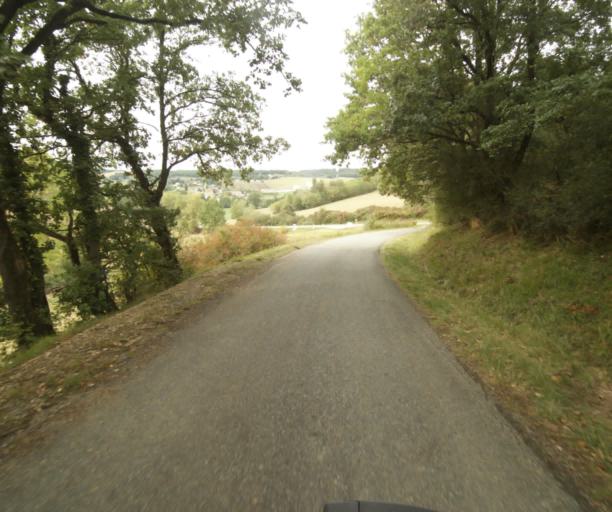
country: FR
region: Midi-Pyrenees
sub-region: Departement du Tarn-et-Garonne
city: Verdun-sur-Garonne
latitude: 43.8569
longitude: 1.1120
